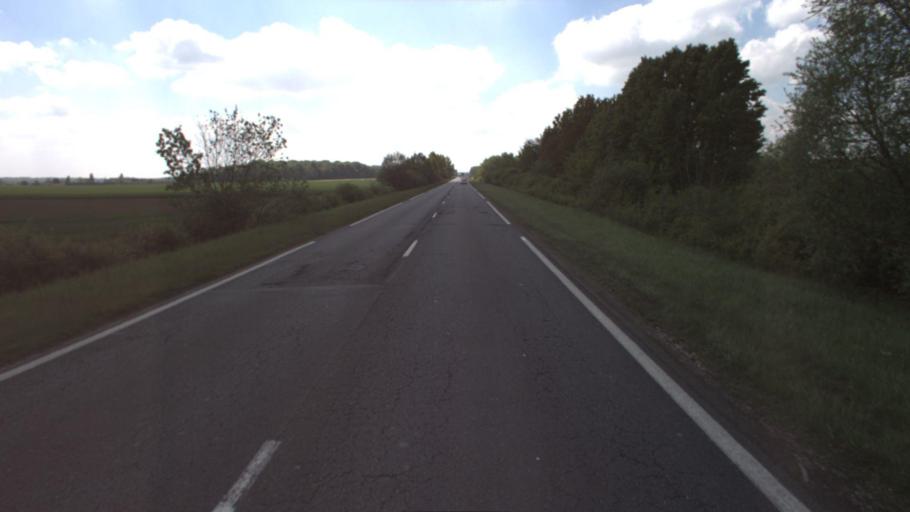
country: FR
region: Ile-de-France
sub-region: Departement de Seine-et-Marne
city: Chaumes-en-Brie
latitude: 48.6801
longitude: 2.8144
